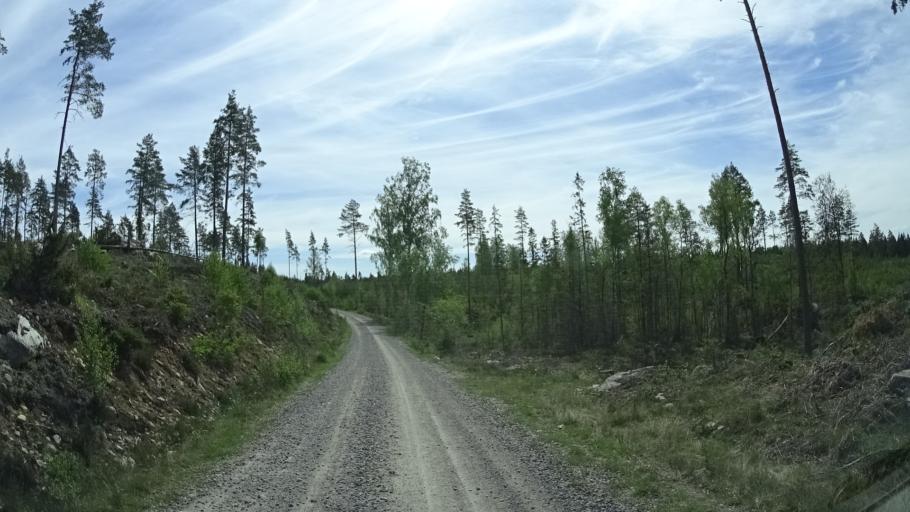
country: SE
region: OEstergoetland
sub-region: Finspangs Kommun
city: Finspang
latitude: 58.7728
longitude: 15.8468
